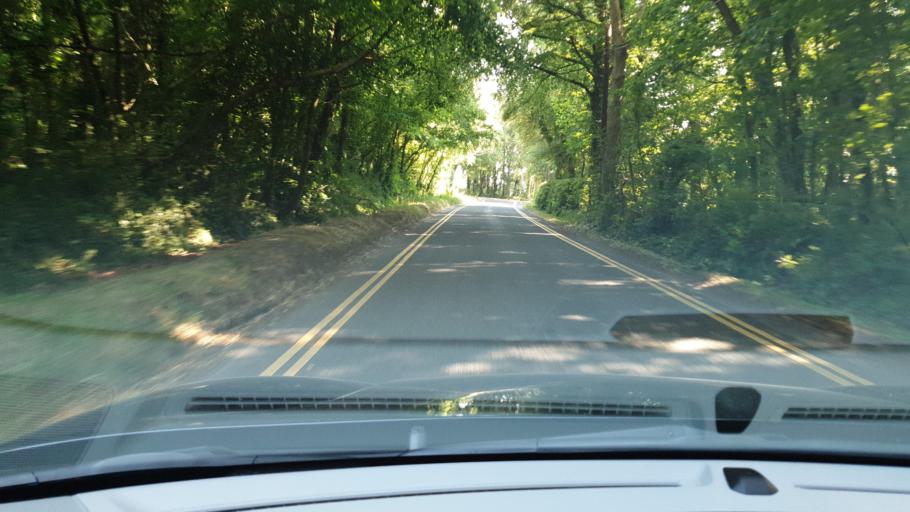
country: IE
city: Kentstown
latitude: 53.6177
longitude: -6.5082
